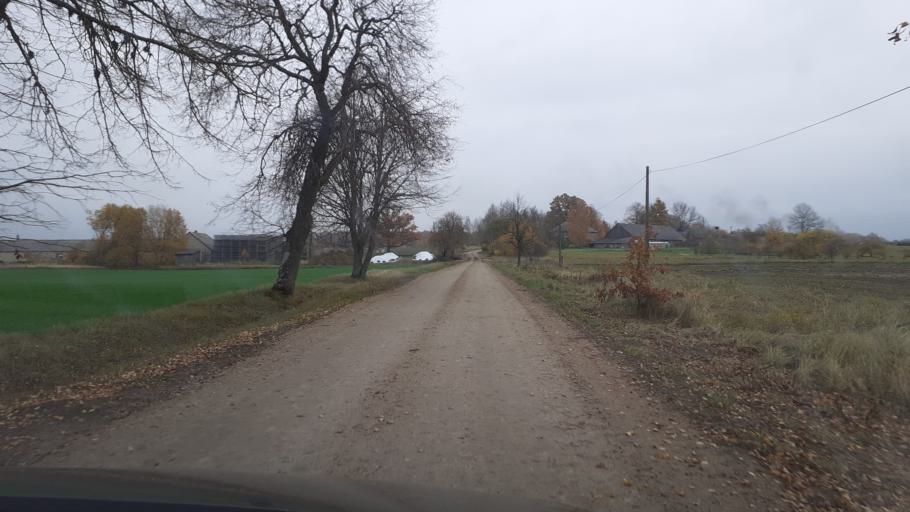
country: LV
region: Skrunda
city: Skrunda
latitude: 56.8543
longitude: 22.2176
